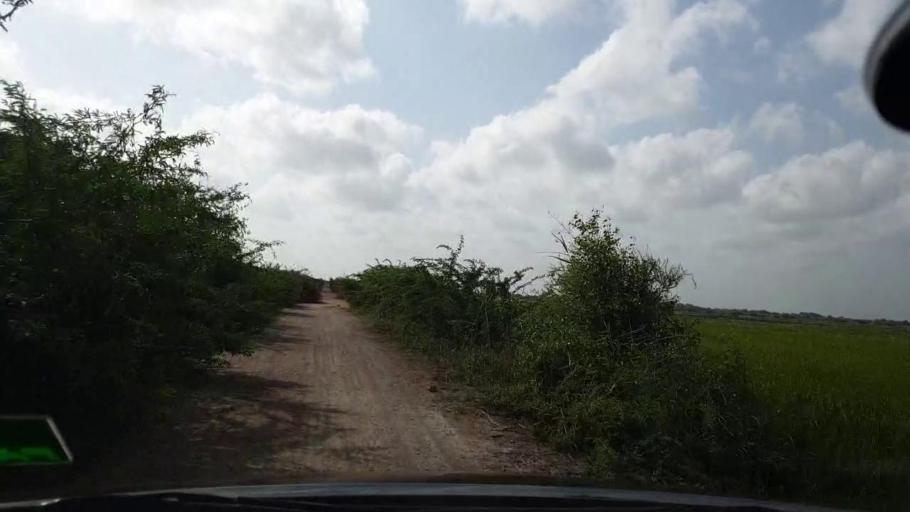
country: PK
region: Sindh
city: Kadhan
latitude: 24.6378
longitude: 69.0875
